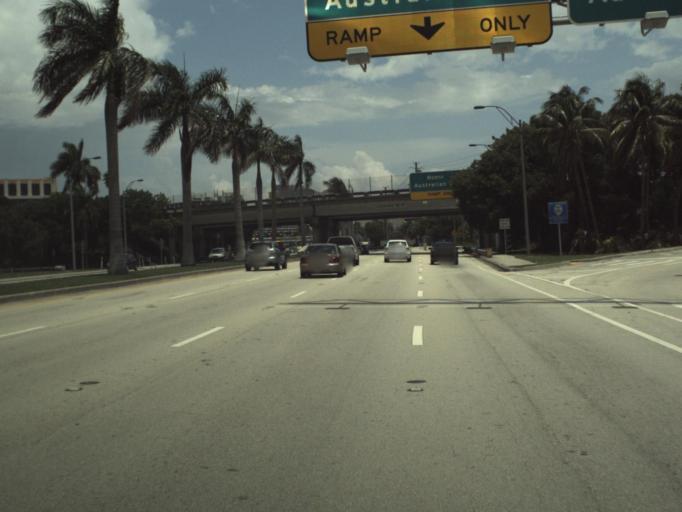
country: US
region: Florida
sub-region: Palm Beach County
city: West Palm Beach
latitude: 26.7056
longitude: -80.0672
